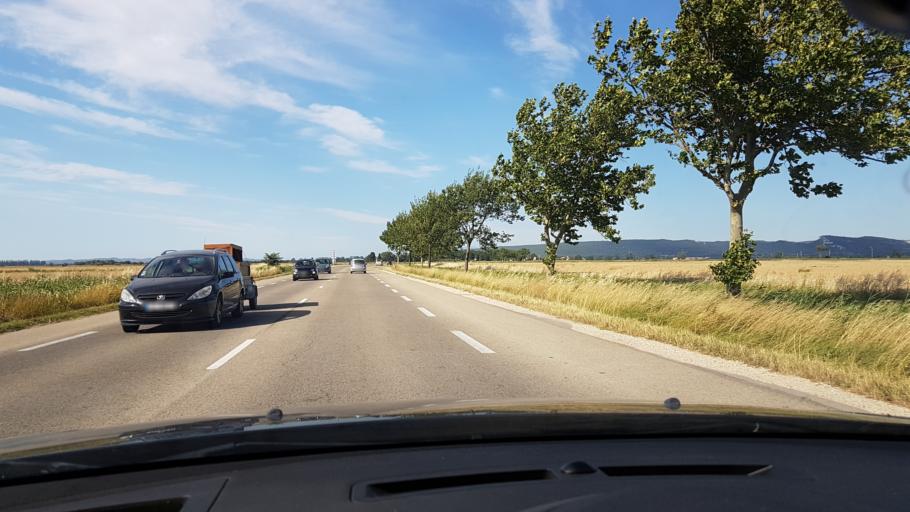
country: FR
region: Languedoc-Roussillon
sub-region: Departement du Gard
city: Fourques
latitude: 43.7224
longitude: 4.6505
